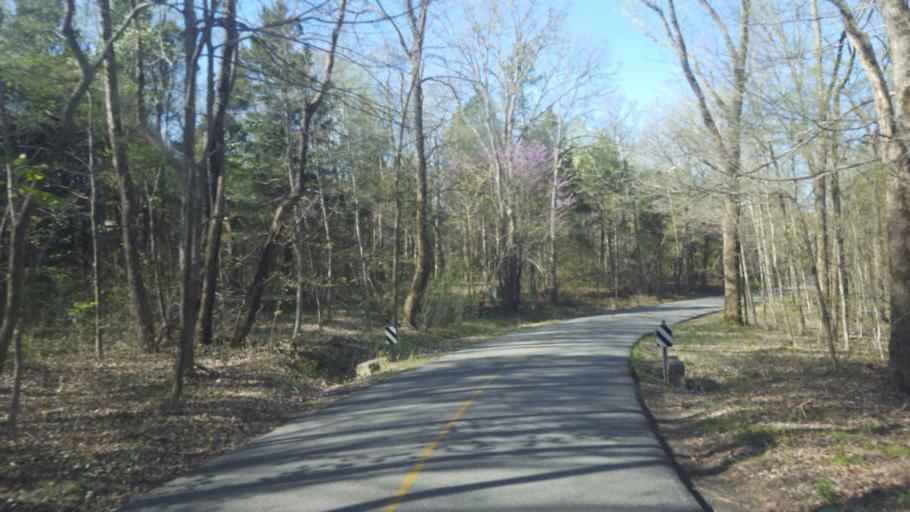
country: US
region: Kentucky
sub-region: Barren County
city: Cave City
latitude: 37.1579
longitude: -86.0465
